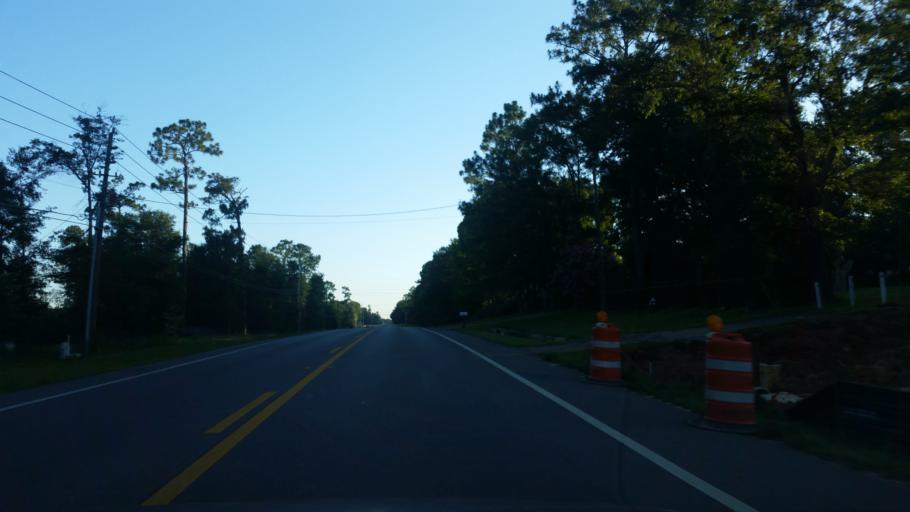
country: US
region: Florida
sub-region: Escambia County
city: Cantonment
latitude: 30.5851
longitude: -87.3282
